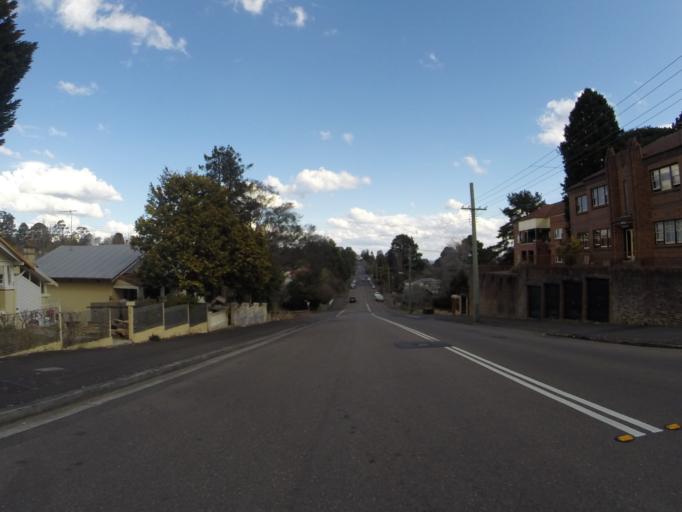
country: AU
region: New South Wales
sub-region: Blue Mountains Municipality
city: Katoomba
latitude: -33.7203
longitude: 150.3103
